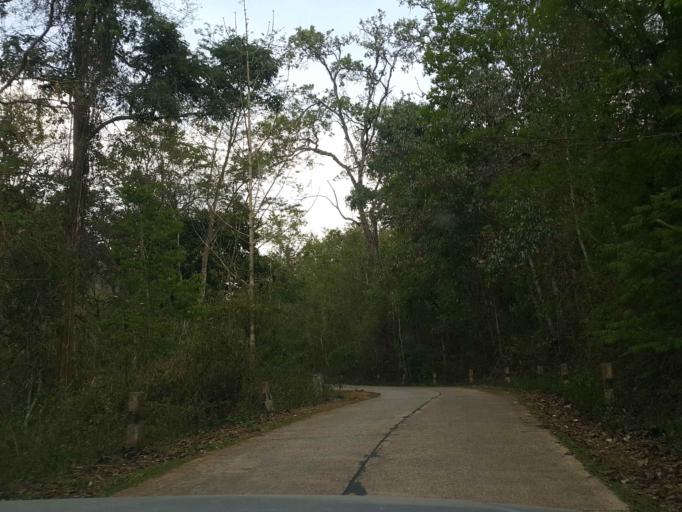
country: TH
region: Chiang Mai
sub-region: Amphoe Chiang Dao
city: Chiang Dao
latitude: 19.3776
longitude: 98.7601
